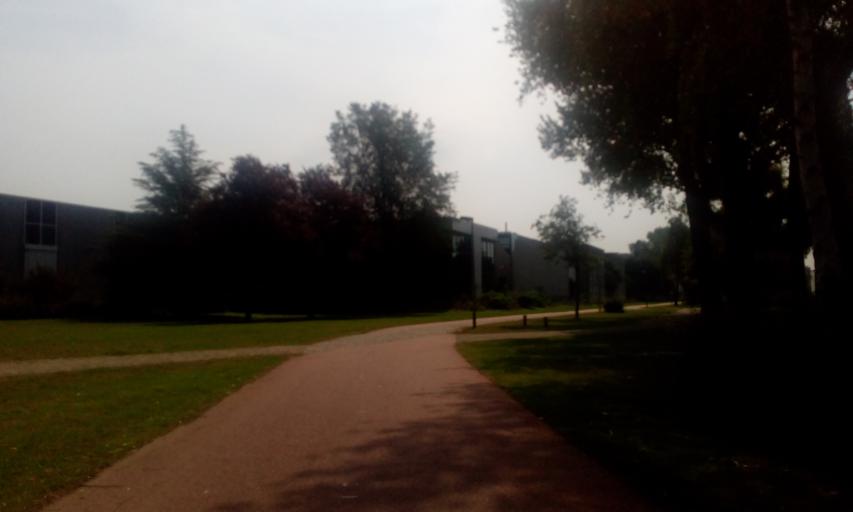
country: NL
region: South Holland
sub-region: Gemeente Capelle aan den IJssel
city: Capelle aan den IJssel
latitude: 51.9601
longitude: 4.5762
